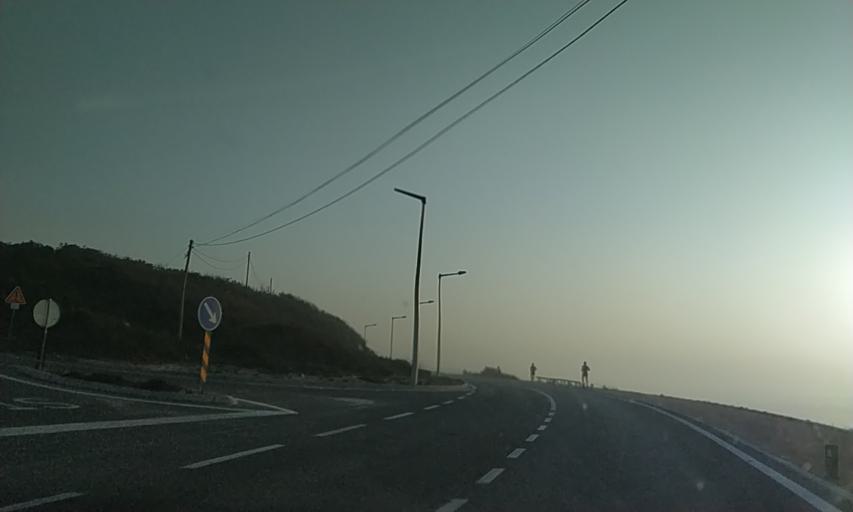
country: PT
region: Leiria
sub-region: Marinha Grande
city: Marinha Grande
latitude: 39.7738
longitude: -9.0229
